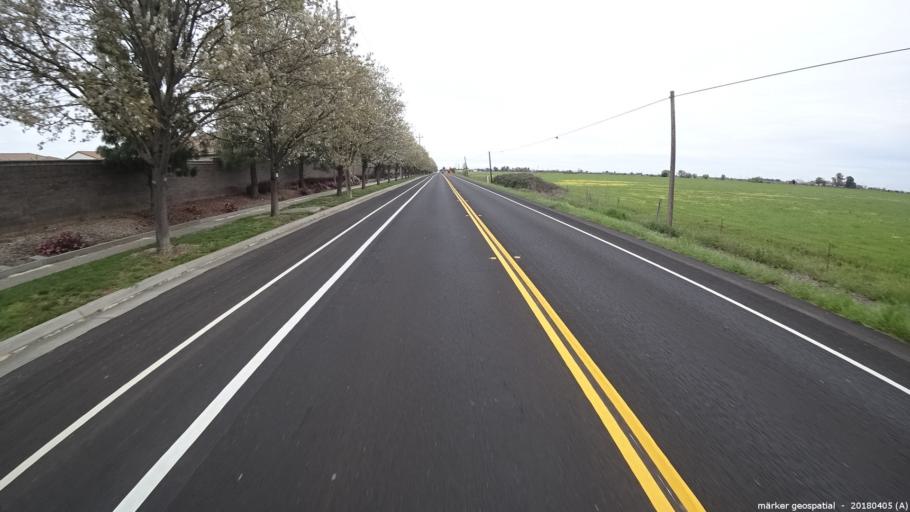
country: US
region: California
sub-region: Sacramento County
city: Laguna
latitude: 38.3794
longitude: -121.4358
